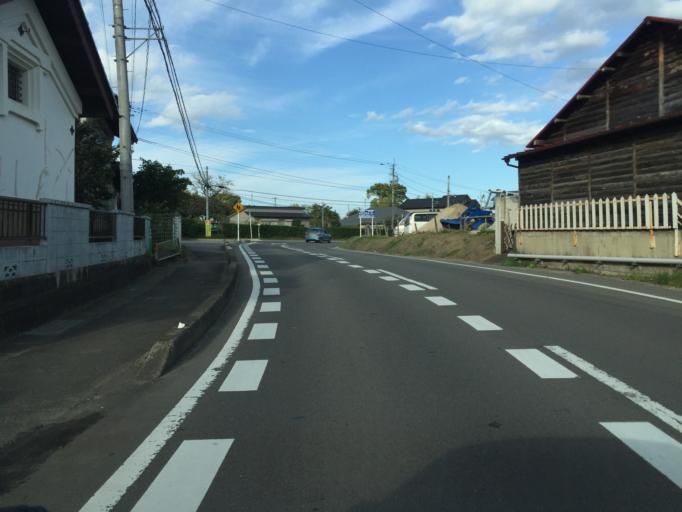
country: JP
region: Fukushima
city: Fukushima-shi
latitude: 37.7083
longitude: 140.4302
